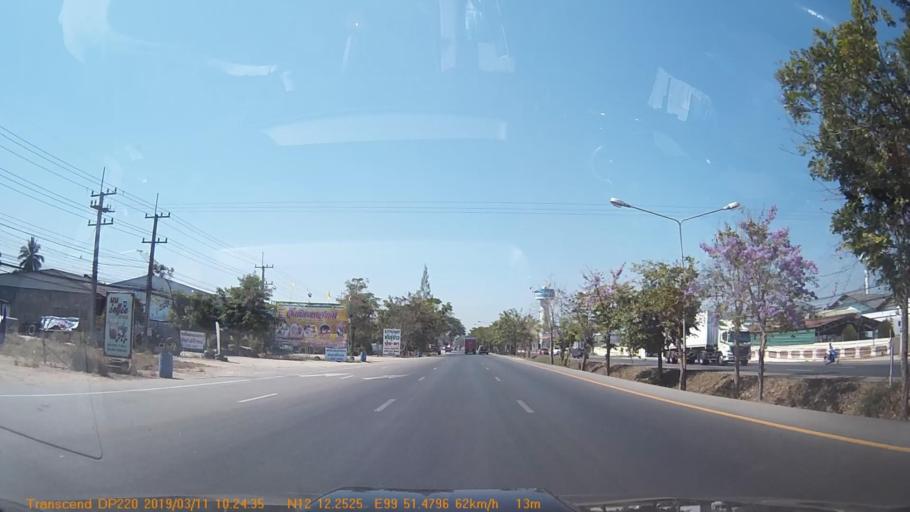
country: TH
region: Prachuap Khiri Khan
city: Sam Roi Yot
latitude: 12.2040
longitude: 99.8579
